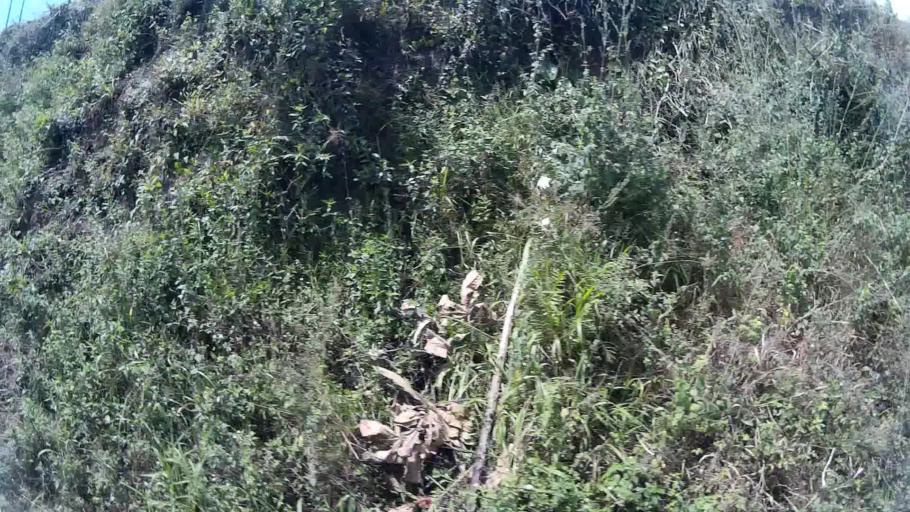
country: CO
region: Caldas
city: Belalcazar
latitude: 4.9700
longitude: -75.8210
